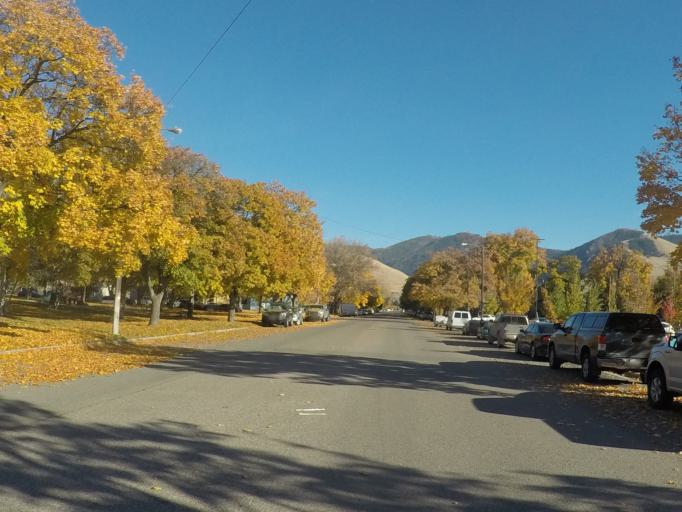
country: US
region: Montana
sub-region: Missoula County
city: Missoula
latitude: 46.8777
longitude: -114.0012
